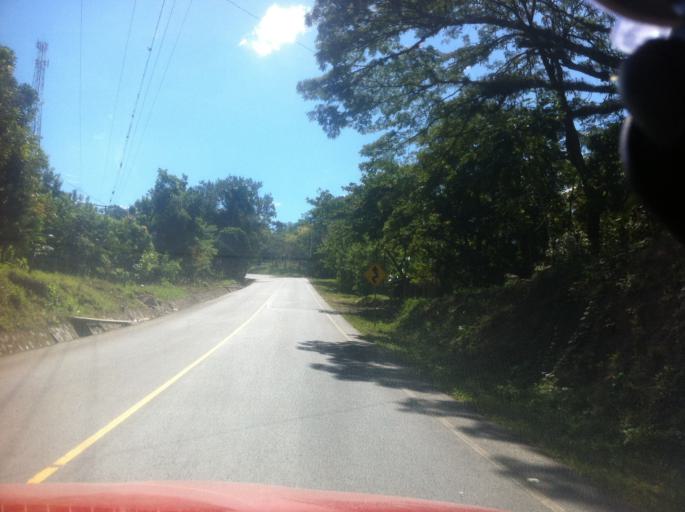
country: NI
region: Matagalpa
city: San Ramon
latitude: 12.8848
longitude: -85.8389
